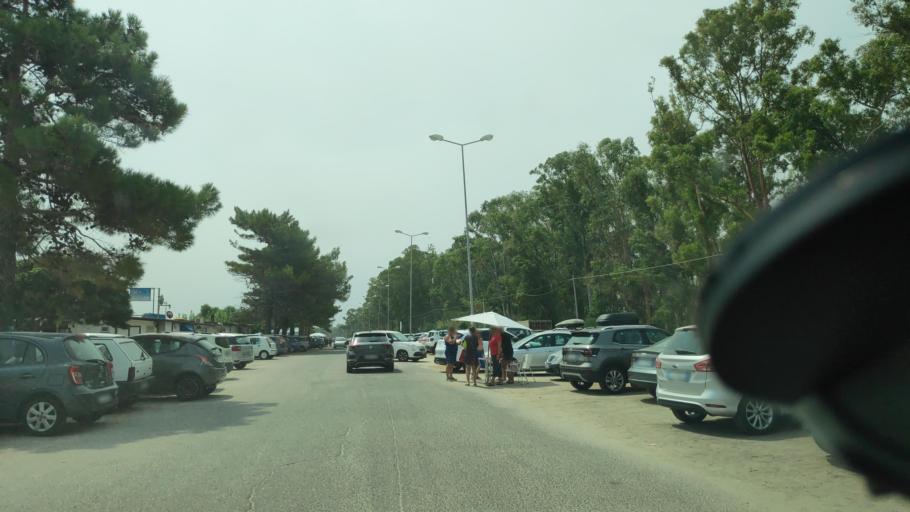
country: IT
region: Calabria
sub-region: Provincia di Catanzaro
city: Sant'Andrea Ionio Marina
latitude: 38.6172
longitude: 16.5603
